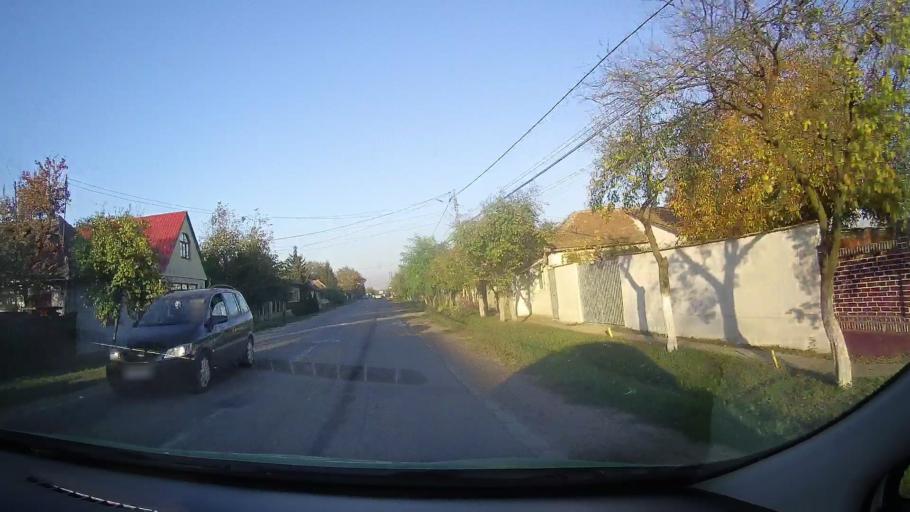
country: RO
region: Bihor
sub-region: Comuna Salard
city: Salard
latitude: 47.2158
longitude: 22.0301
